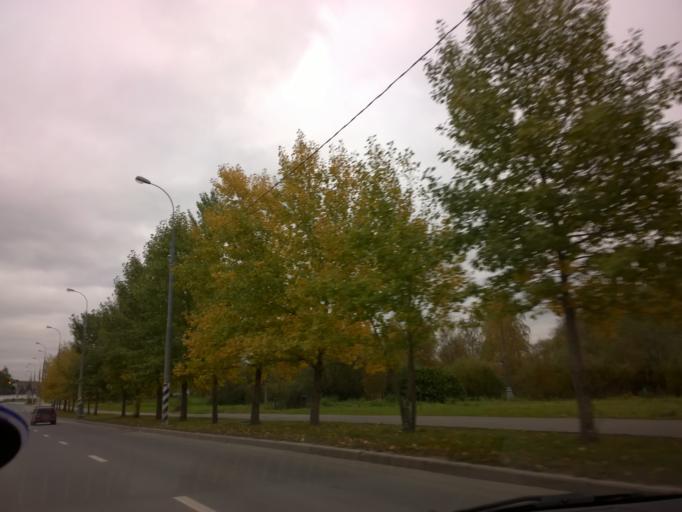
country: RU
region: Moskovskaya
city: Kommunarka
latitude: 55.5384
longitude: 37.4994
